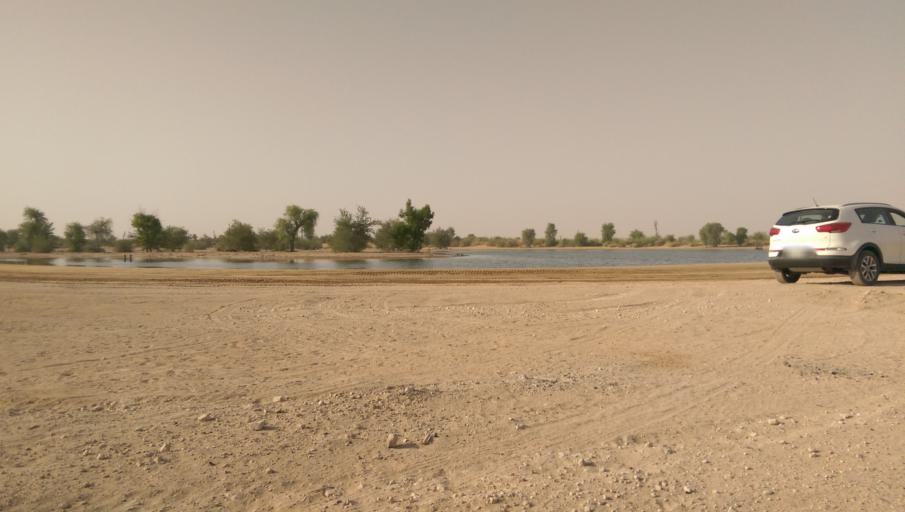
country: AE
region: Dubai
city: Dubai
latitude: 24.8380
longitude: 55.3752
